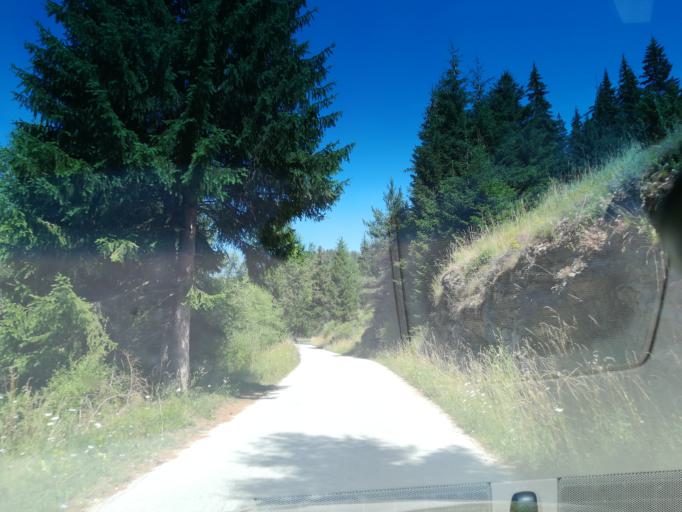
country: BG
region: Smolyan
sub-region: Obshtina Chepelare
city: Chepelare
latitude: 41.6710
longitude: 24.7930
